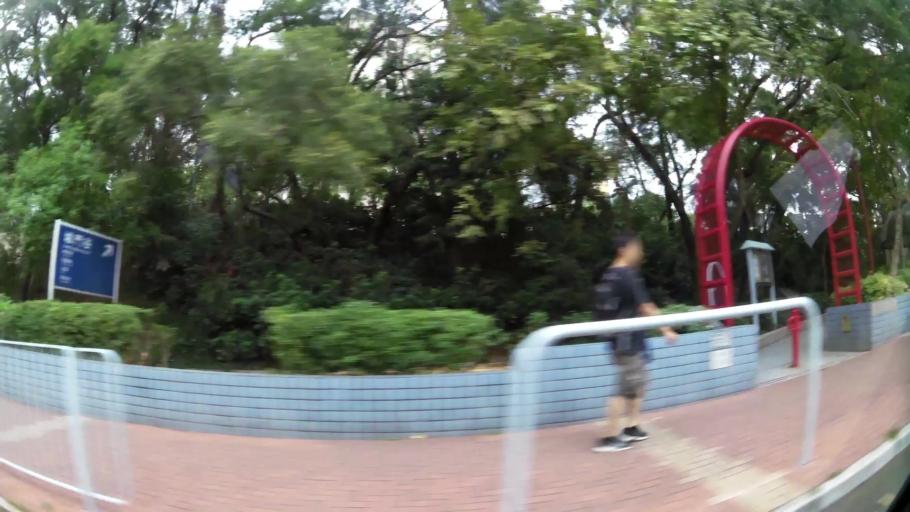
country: HK
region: Tsuen Wan
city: Tsuen Wan
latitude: 22.3733
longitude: 114.1223
